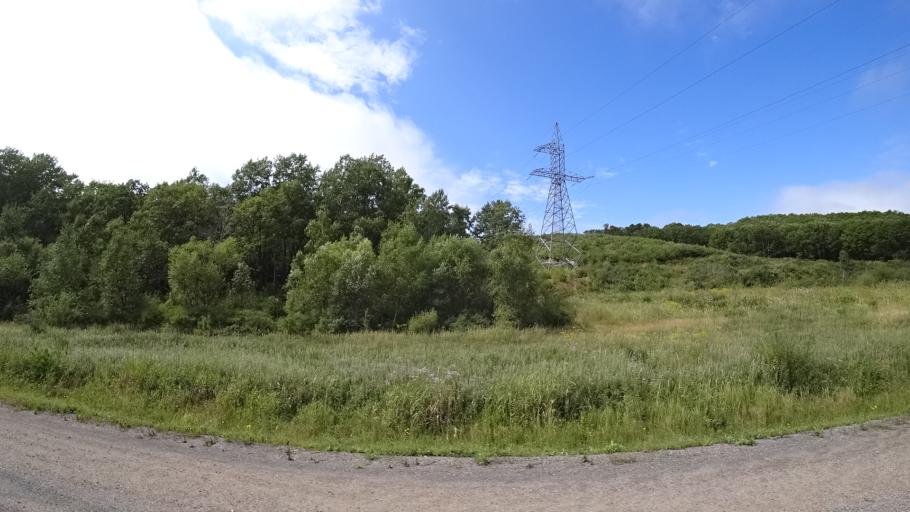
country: RU
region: Primorskiy
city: Lyalichi
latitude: 44.1213
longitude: 132.4205
